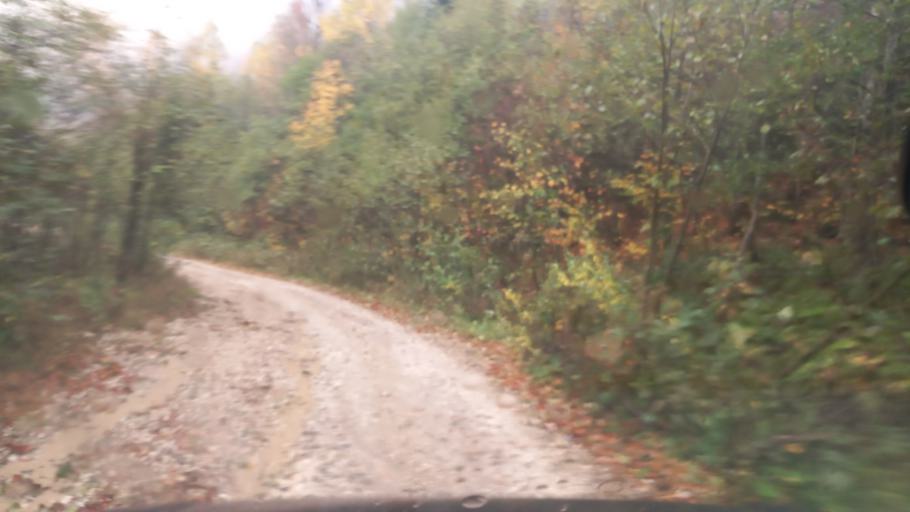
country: RU
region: Krasnodarskiy
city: Neftegorsk
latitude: 44.0105
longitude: 39.8409
